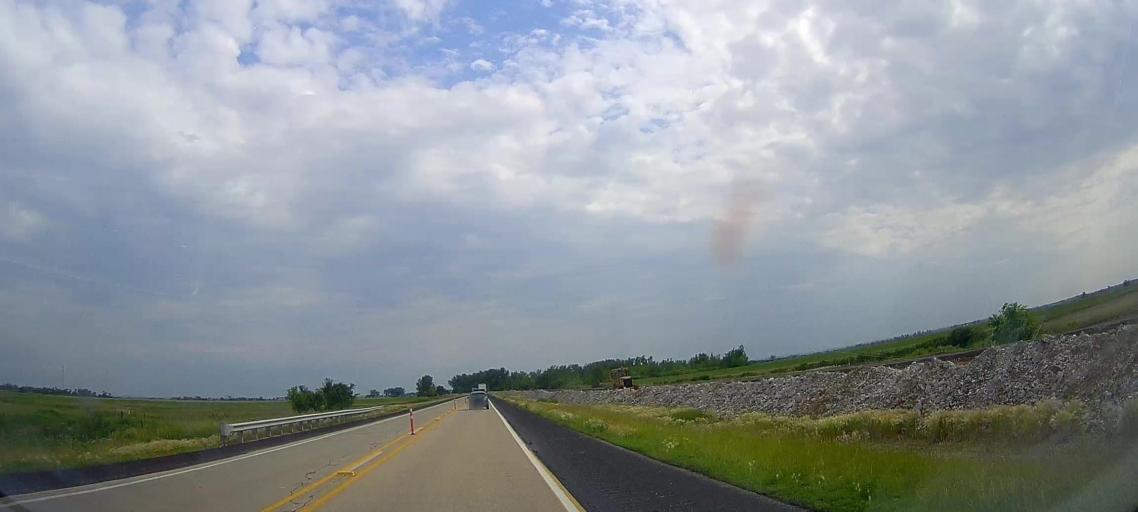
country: US
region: Nebraska
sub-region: Washington County
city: Blair
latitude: 41.6861
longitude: -96.0413
